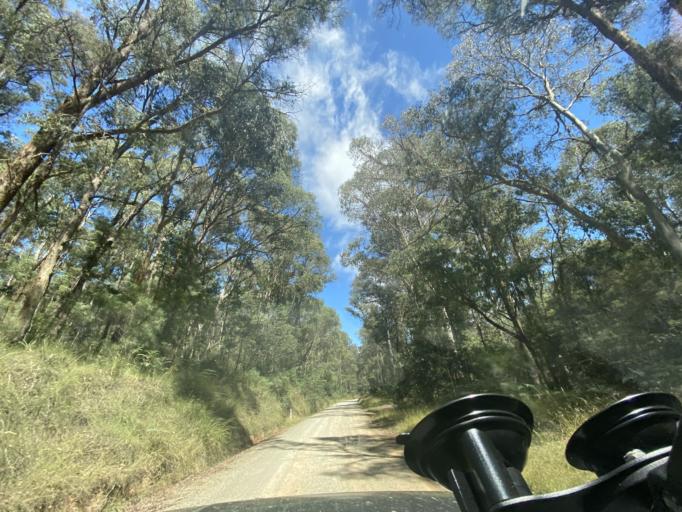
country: AU
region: Victoria
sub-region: Yarra Ranges
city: Millgrove
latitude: -37.5296
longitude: 145.9888
